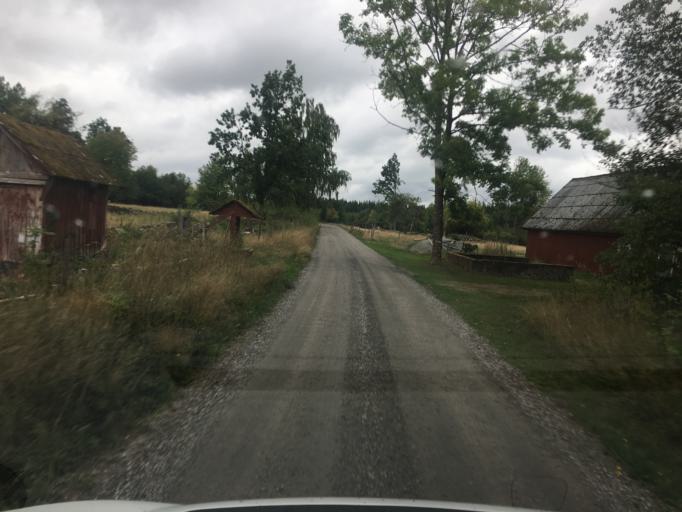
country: SE
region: Kronoberg
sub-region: Ljungby Kommun
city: Lagan
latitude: 56.9622
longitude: 14.0446
